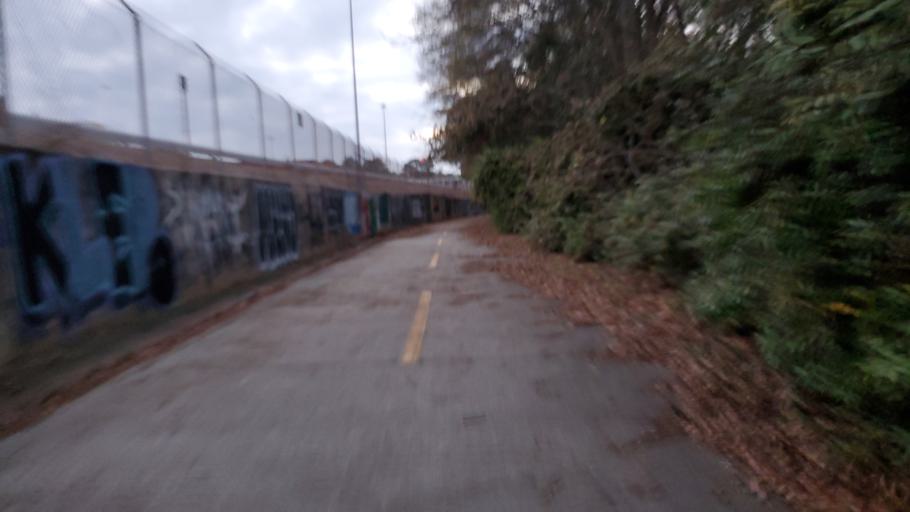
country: US
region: Georgia
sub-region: DeKalb County
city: Avondale Estates
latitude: 33.7795
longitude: -84.2705
